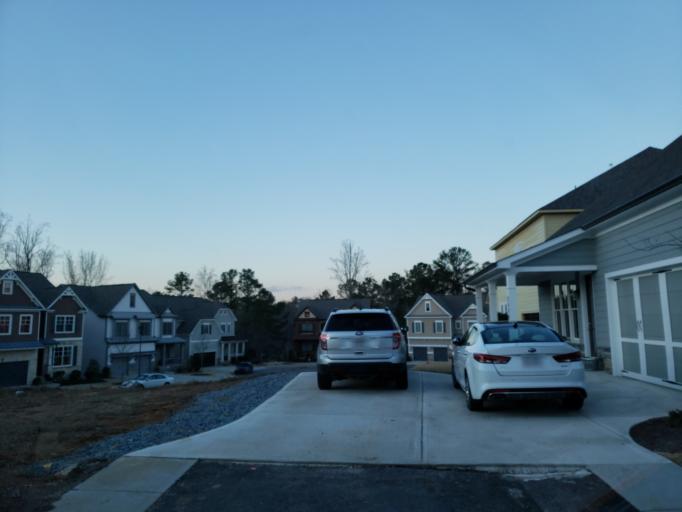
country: US
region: Georgia
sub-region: Cherokee County
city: Woodstock
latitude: 34.0980
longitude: -84.4962
